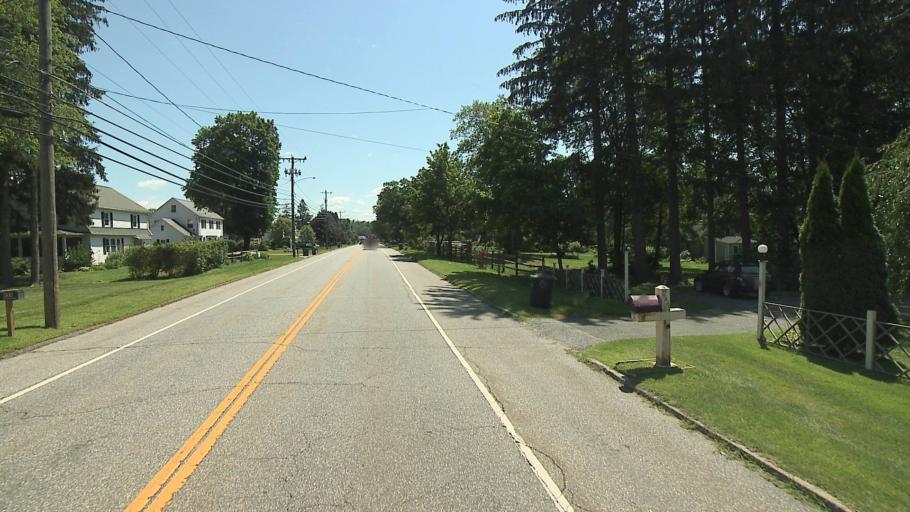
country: US
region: Connecticut
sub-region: Litchfield County
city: Torrington
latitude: 41.8046
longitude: -73.0935
